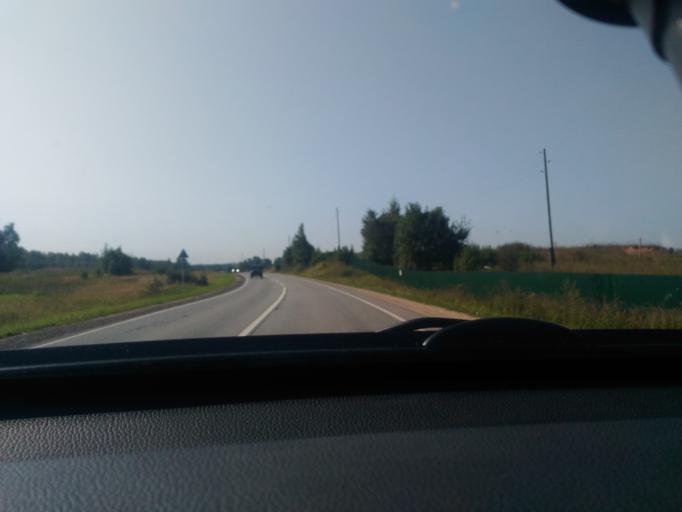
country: RU
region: Moskovskaya
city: Podosinki
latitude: 56.2266
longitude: 37.5483
